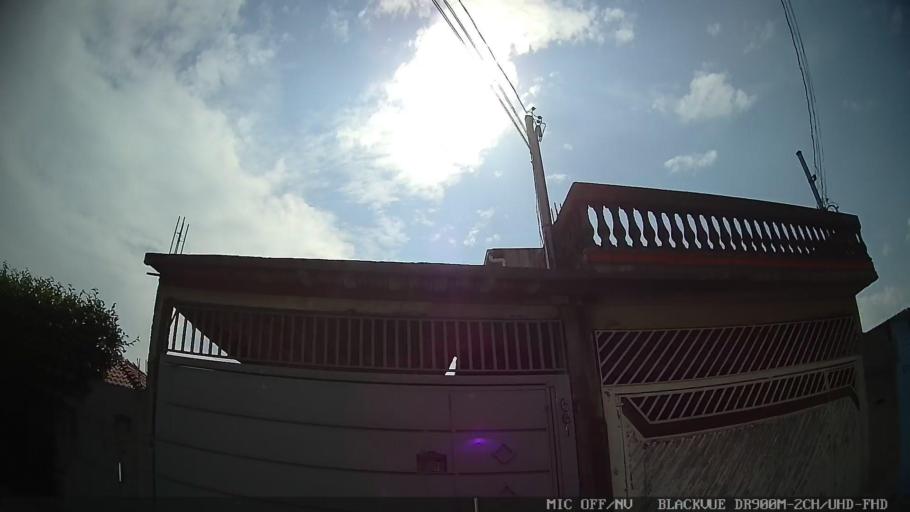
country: BR
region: Sao Paulo
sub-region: Ferraz De Vasconcelos
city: Ferraz de Vasconcelos
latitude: -23.5029
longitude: -46.4153
